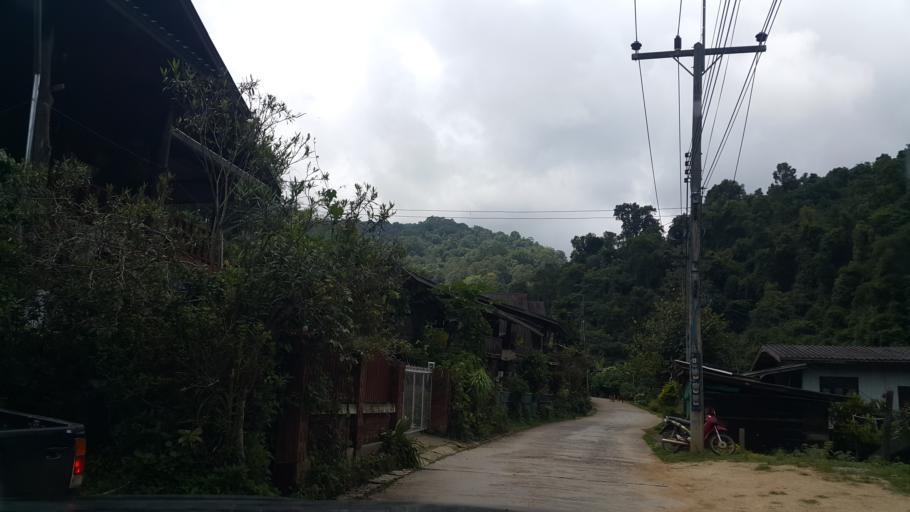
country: TH
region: Lampang
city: Wang Nuea
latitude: 19.0883
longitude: 99.3755
